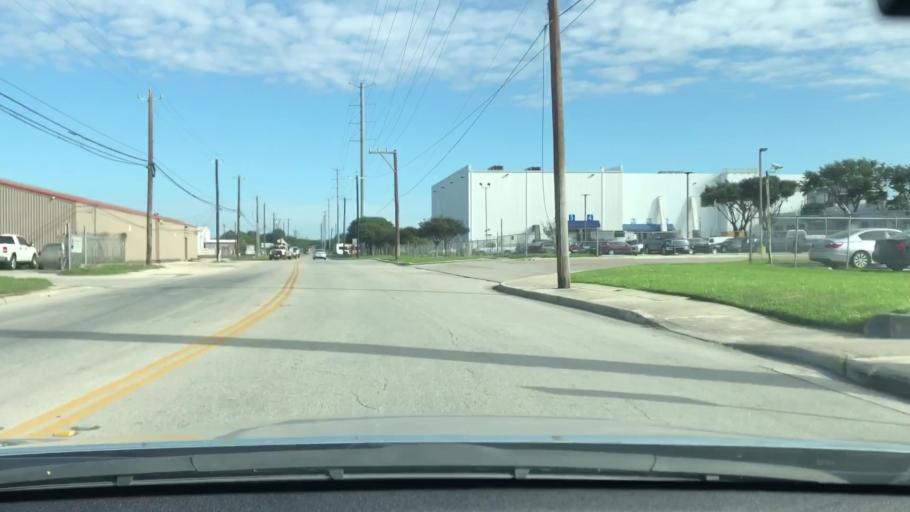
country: US
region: Texas
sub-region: Bexar County
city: Kirby
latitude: 29.4852
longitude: -98.3927
